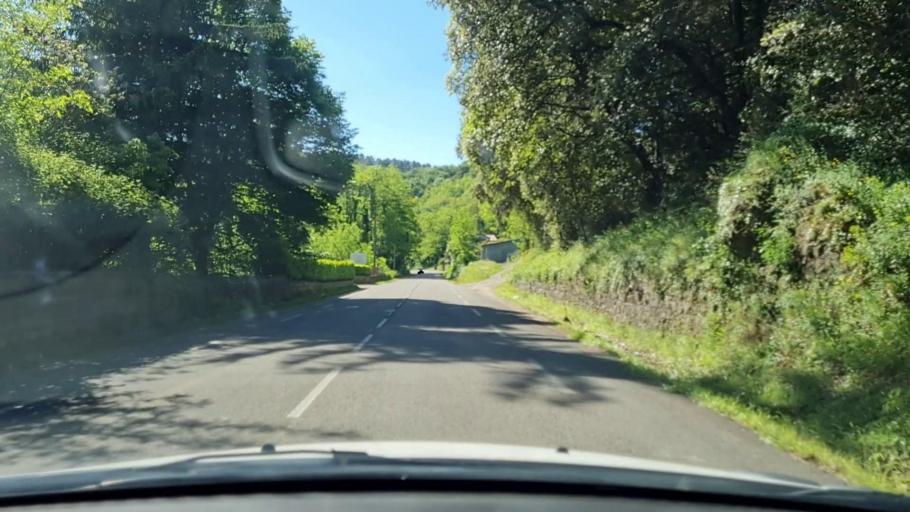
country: FR
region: Languedoc-Roussillon
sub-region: Departement du Gard
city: Cendras
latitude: 44.1457
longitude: 4.0616
